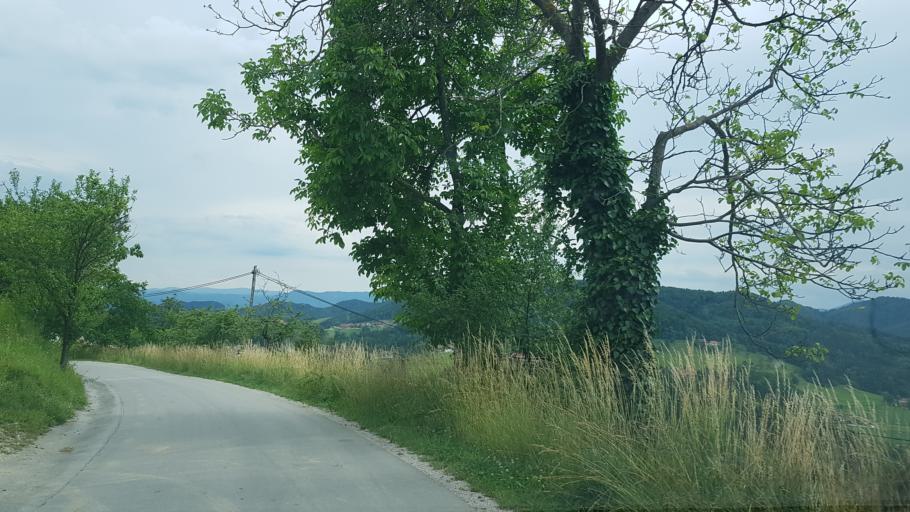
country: SI
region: Dobrna
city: Dobrna
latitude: 46.3478
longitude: 15.2395
